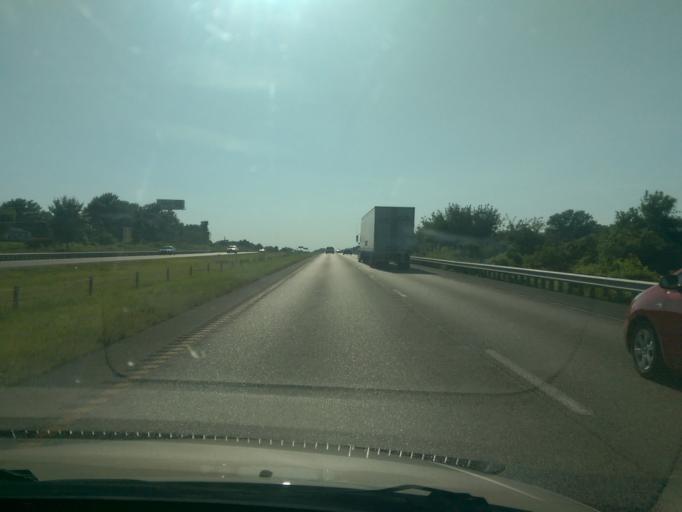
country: US
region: Missouri
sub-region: Lafayette County
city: Odessa
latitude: 39.0071
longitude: -93.9246
